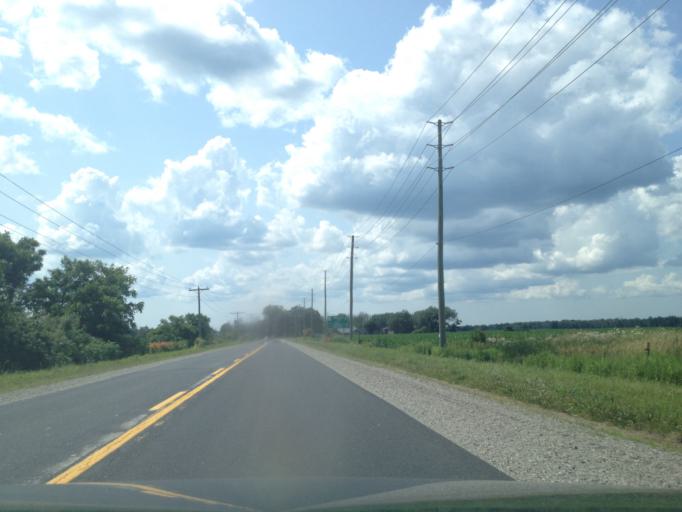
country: CA
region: Ontario
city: Aylmer
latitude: 42.6727
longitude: -80.8551
